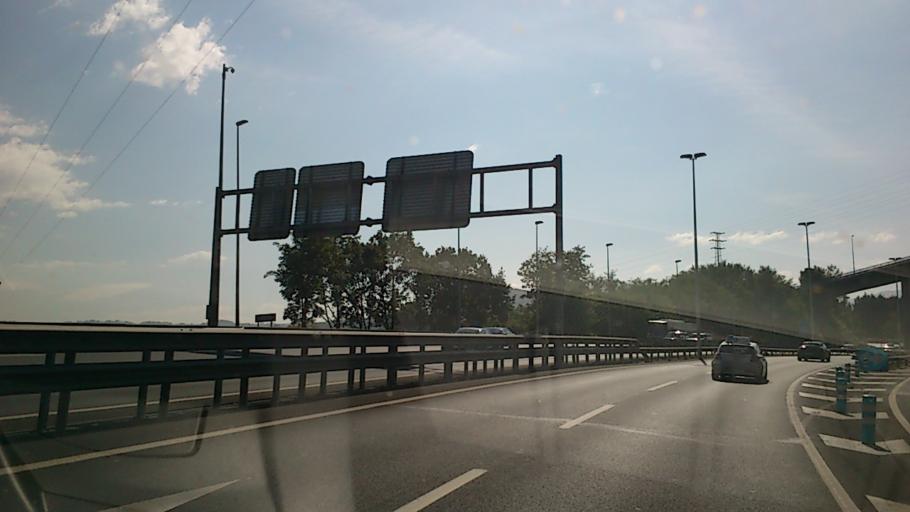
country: ES
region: Basque Country
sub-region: Bizkaia
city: Erandio
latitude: 43.3055
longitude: -2.9613
